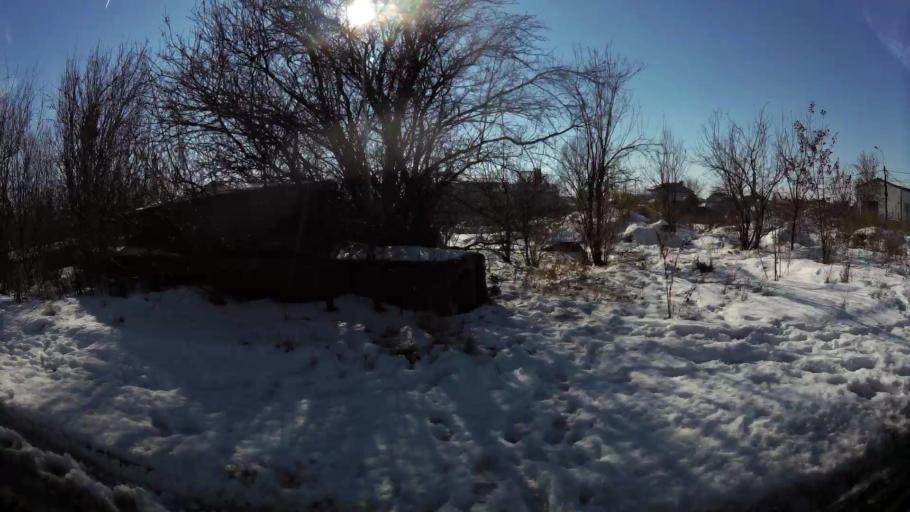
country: RO
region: Ilfov
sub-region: Comuna Magurele
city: Magurele
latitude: 44.3832
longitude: 26.0474
